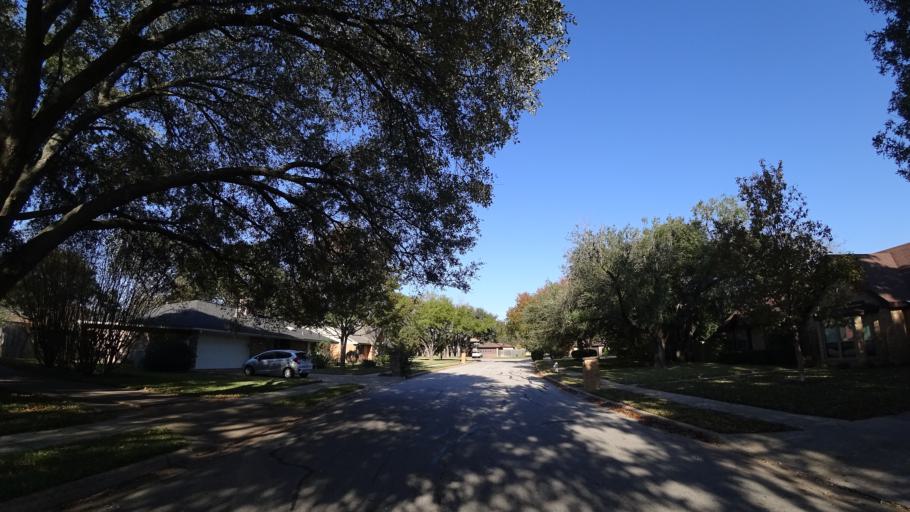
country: US
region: Texas
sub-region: Travis County
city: Shady Hollow
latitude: 30.2198
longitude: -97.8523
